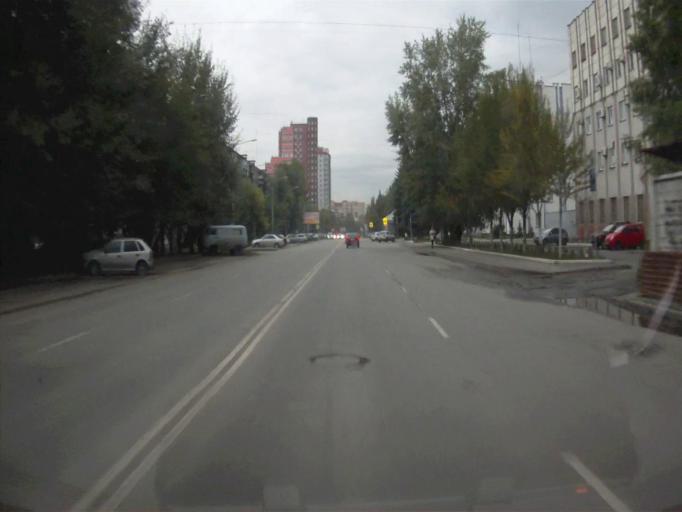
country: RU
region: Chelyabinsk
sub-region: Gorod Chelyabinsk
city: Chelyabinsk
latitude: 55.1485
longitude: 61.3987
